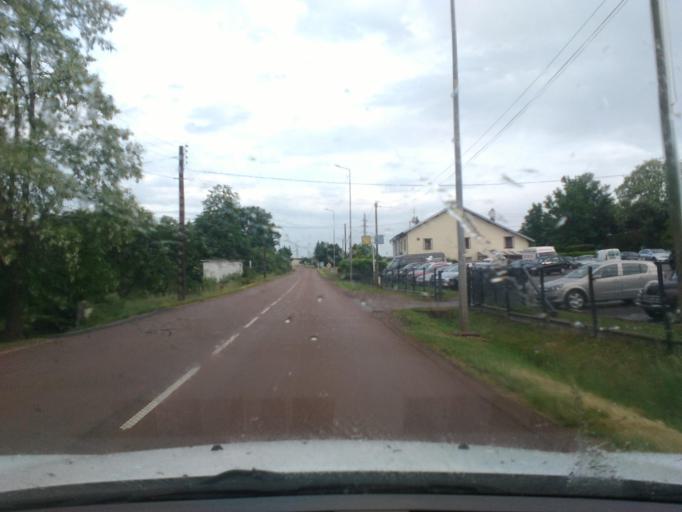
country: FR
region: Lorraine
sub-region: Departement des Vosges
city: Rambervillers
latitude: 48.3577
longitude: 6.6289
